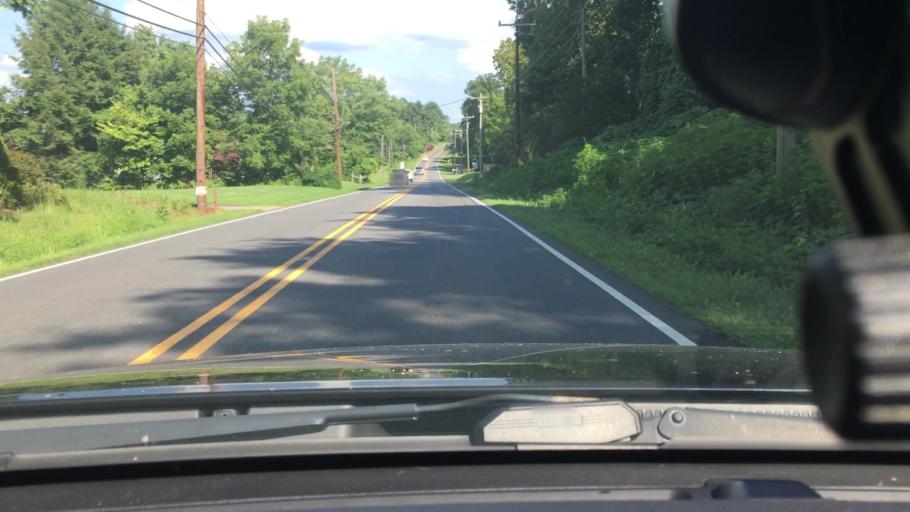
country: US
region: North Carolina
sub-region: Rutherford County
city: Rutherfordton
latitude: 35.3925
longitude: -81.9831
